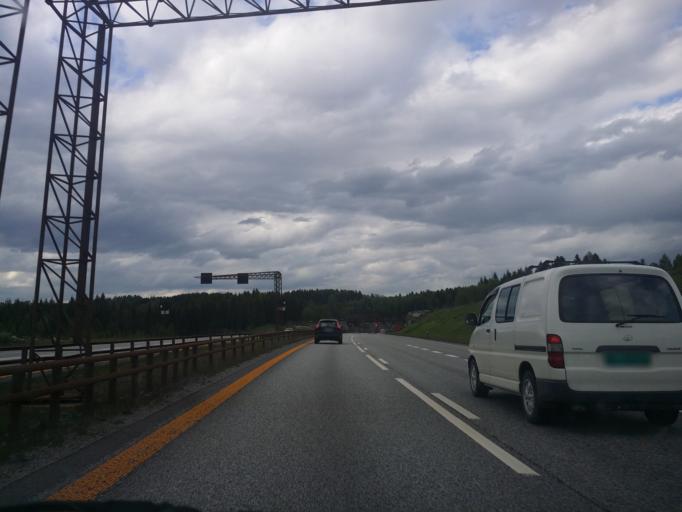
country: NO
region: Akershus
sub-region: Eidsvoll
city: Raholt
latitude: 60.3330
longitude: 11.1913
